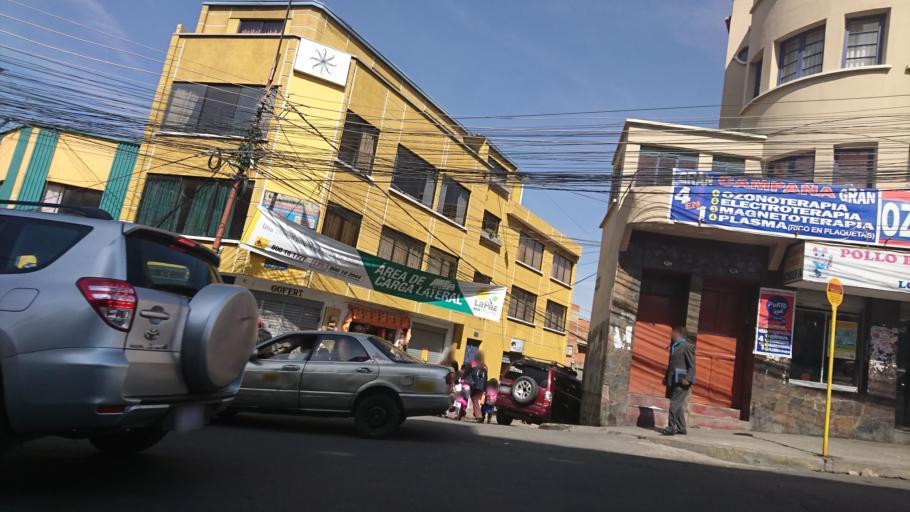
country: BO
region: La Paz
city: La Paz
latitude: -16.4975
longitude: -68.1280
